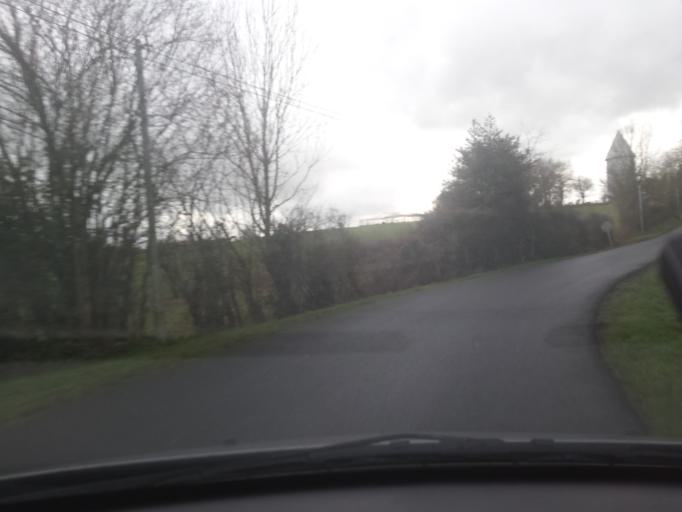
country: FR
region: Pays de la Loire
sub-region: Departement de la Vendee
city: Chambretaud
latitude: 46.9053
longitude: -0.9896
